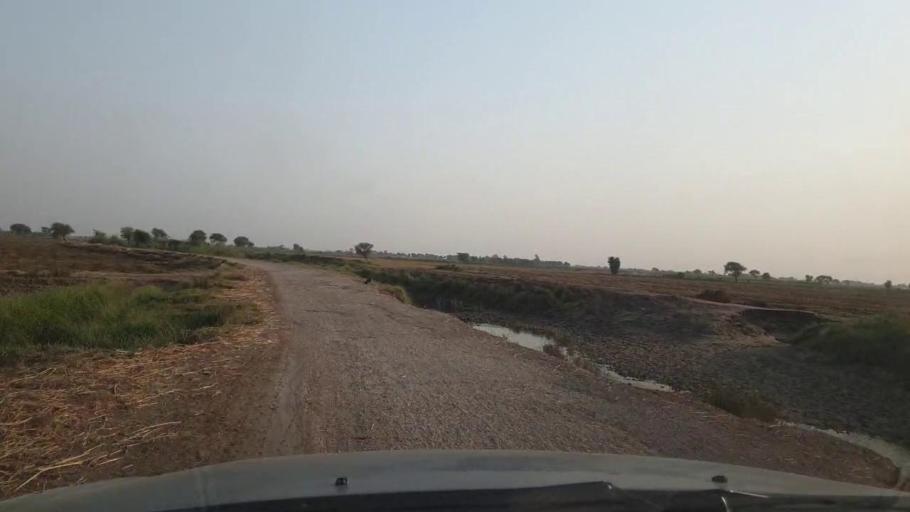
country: PK
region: Sindh
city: Tando Muhammad Khan
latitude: 25.0273
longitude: 68.4371
